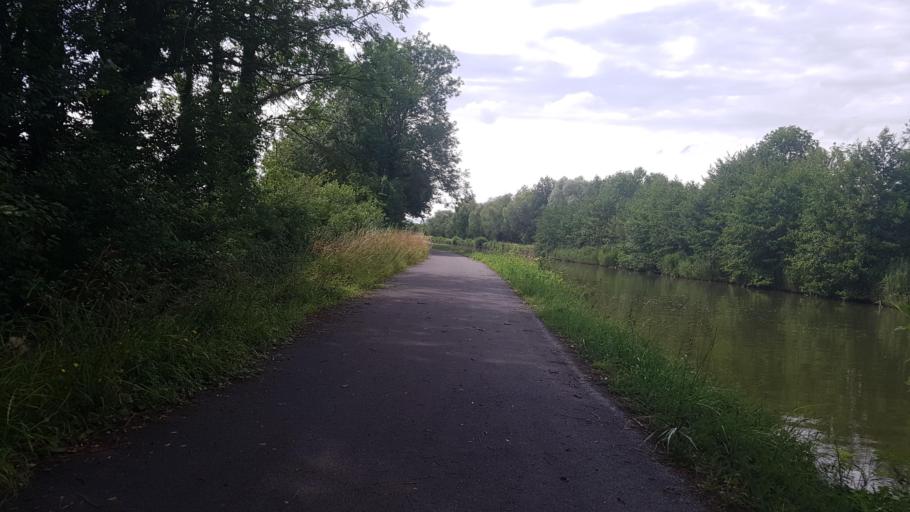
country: FR
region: Lorraine
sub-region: Departement de la Moselle
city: Dieuze
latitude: 48.6854
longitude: 6.7766
